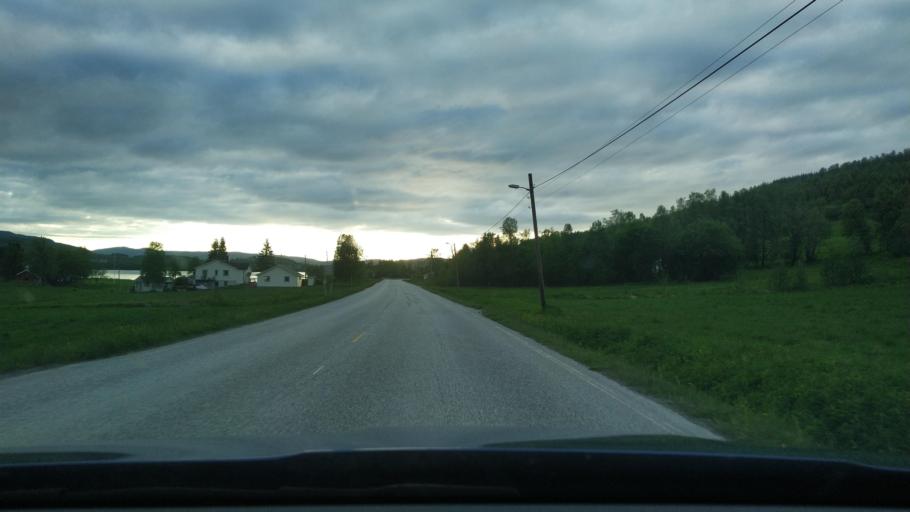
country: NO
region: Troms
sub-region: Sorreisa
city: Sorreisa
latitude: 69.1275
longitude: 18.2106
